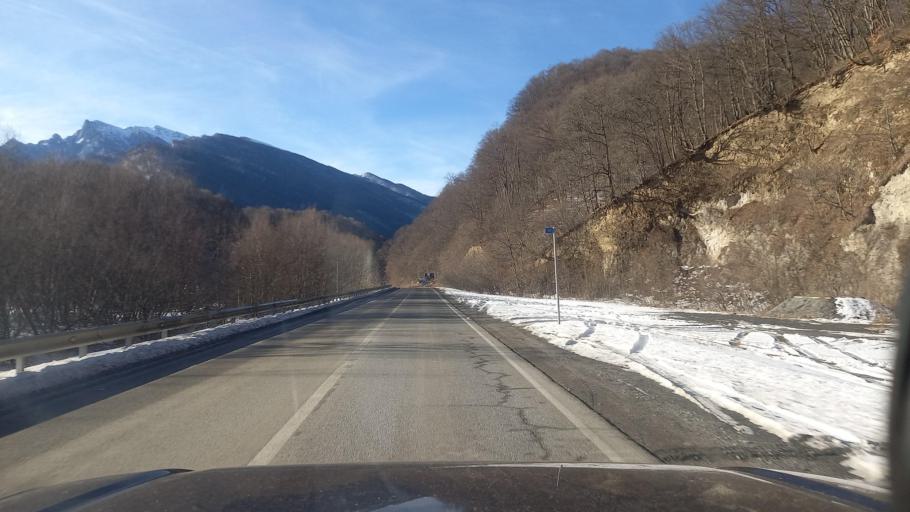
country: RU
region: North Ossetia
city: Gizel'
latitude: 42.9298
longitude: 44.5428
